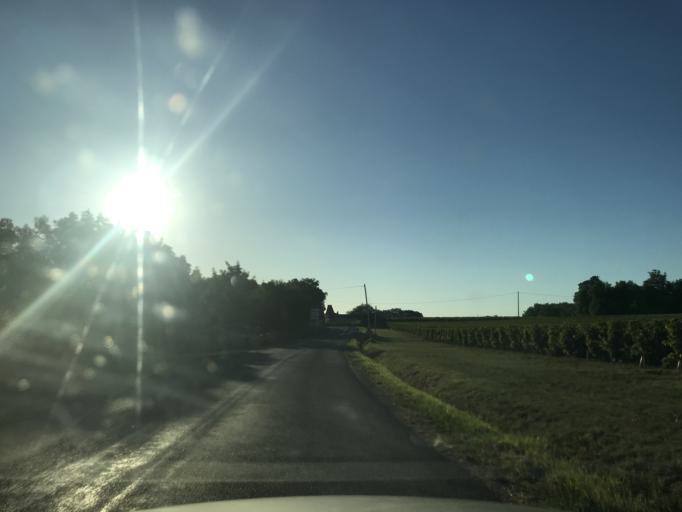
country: FR
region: Aquitaine
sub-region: Departement de la Gironde
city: Mouliets-et-Villemartin
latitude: 44.8935
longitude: -0.0465
